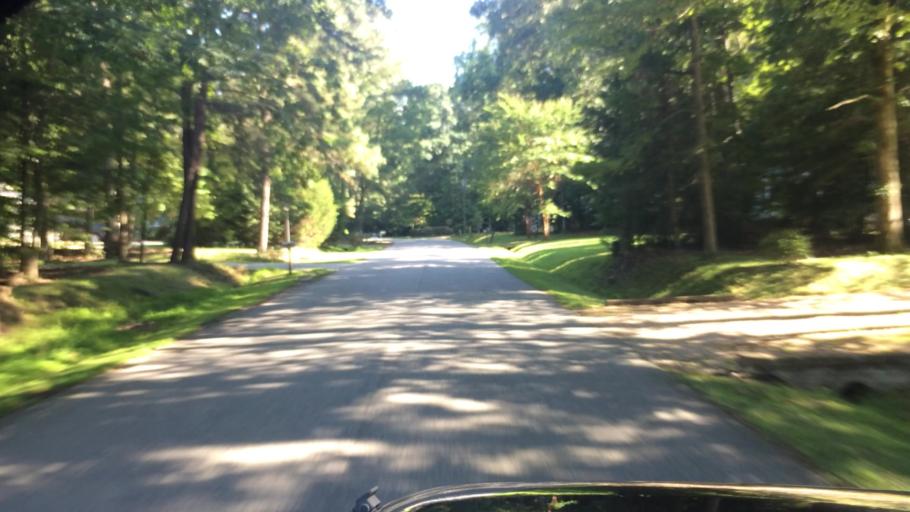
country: US
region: Virginia
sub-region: James City County
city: Williamsburg
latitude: 37.2420
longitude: -76.7981
